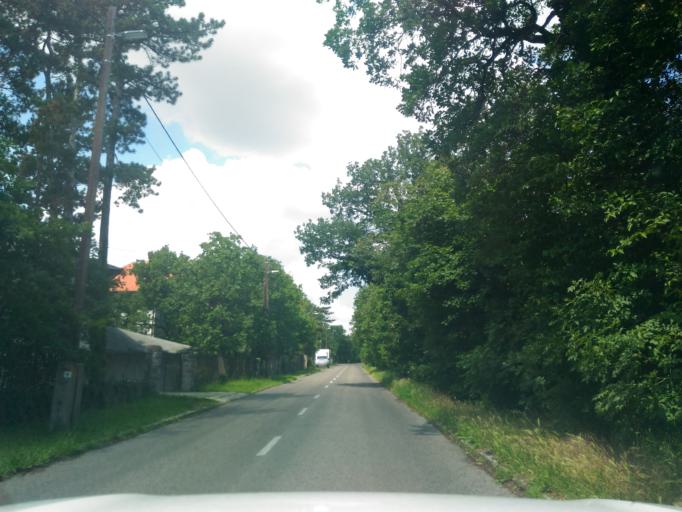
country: HU
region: Baranya
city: Pecs
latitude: 46.0918
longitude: 18.2290
